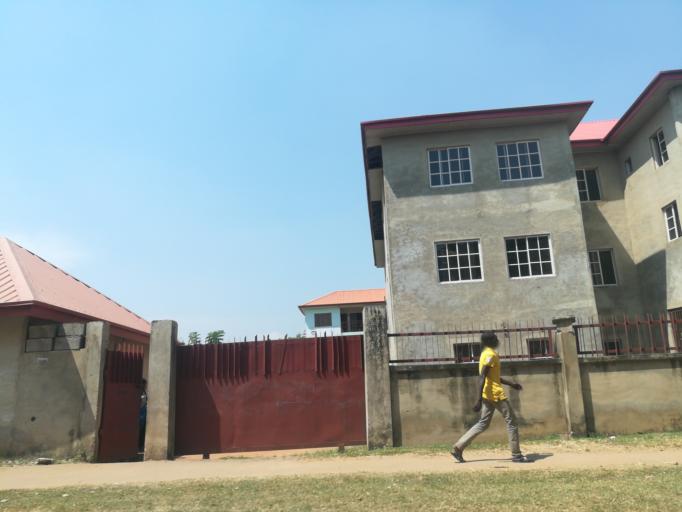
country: NG
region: Abuja Federal Capital Territory
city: Abuja
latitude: 9.0727
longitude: 7.4500
